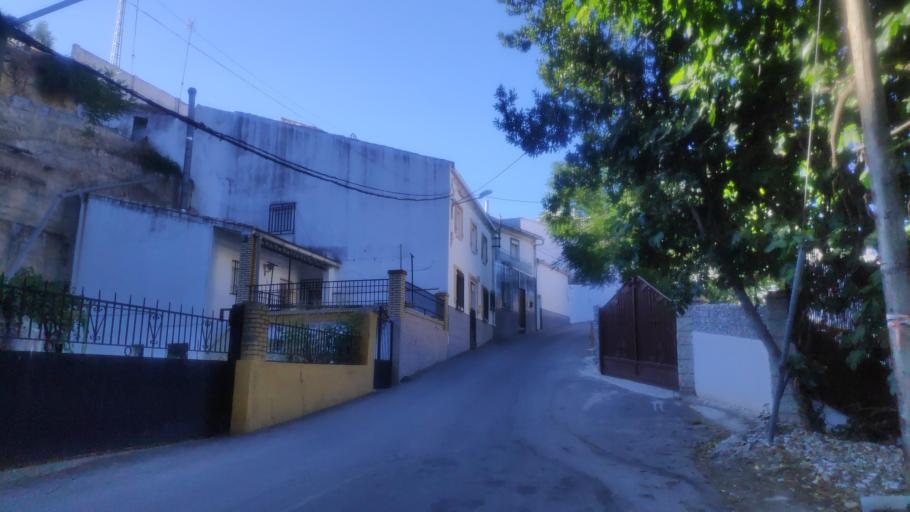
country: ES
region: Andalusia
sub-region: Provincia de Jaen
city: Pozo Alcon
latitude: 37.6732
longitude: -2.9720
